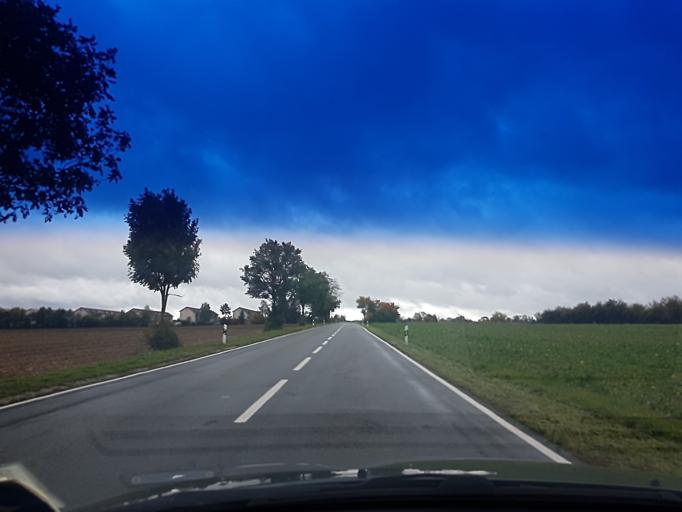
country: DE
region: Bavaria
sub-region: Upper Franconia
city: Bindlach
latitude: 50.0002
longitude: 11.6237
